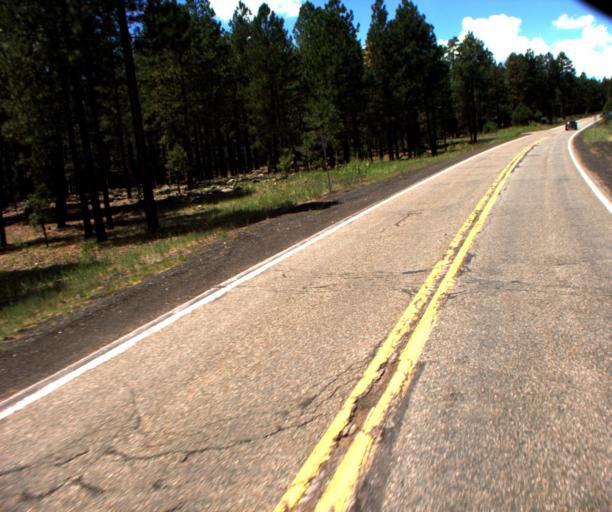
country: US
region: Arizona
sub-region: Coconino County
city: Flagstaff
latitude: 35.2863
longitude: -111.7582
